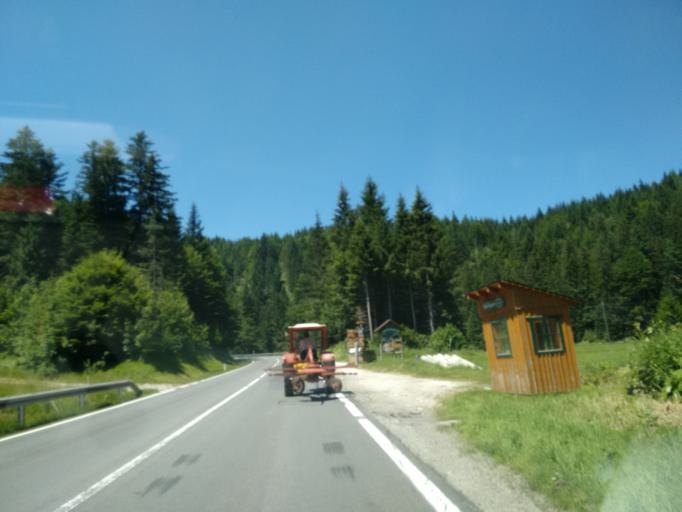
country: AT
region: Styria
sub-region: Politischer Bezirk Liezen
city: Altaussee
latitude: 47.6272
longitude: 13.7088
